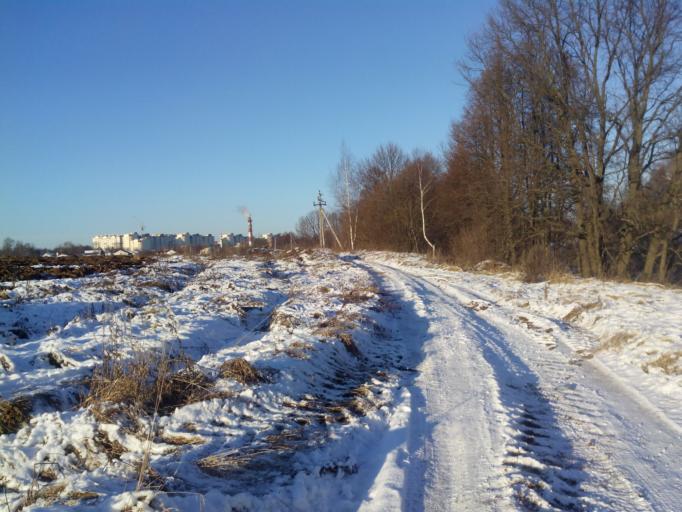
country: RU
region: Moskovskaya
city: Yakovlevskoye
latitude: 55.4944
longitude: 37.9537
